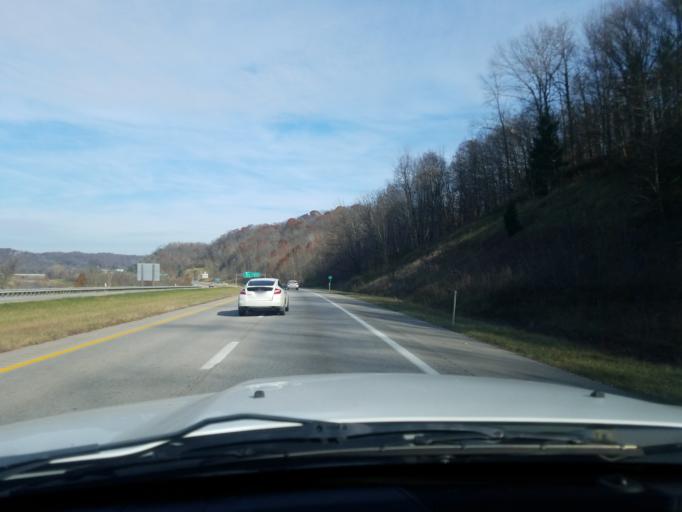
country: US
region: Ohio
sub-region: Athens County
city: Athens
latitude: 39.3165
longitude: -82.0937
